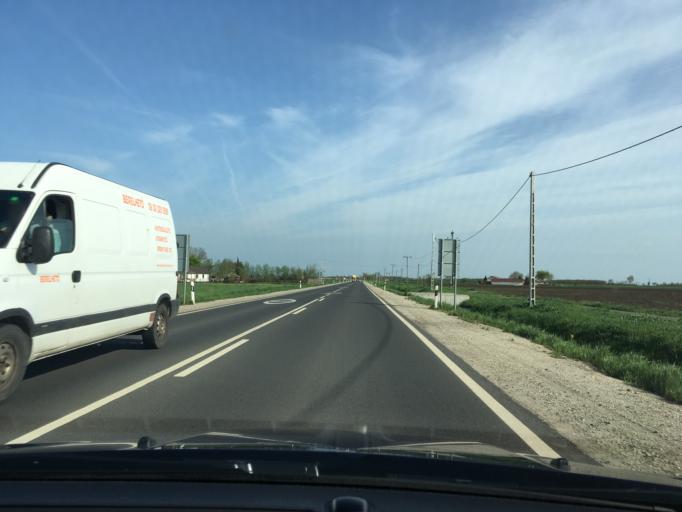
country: HU
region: Bekes
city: Csorvas
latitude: 46.6448
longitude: 20.8746
